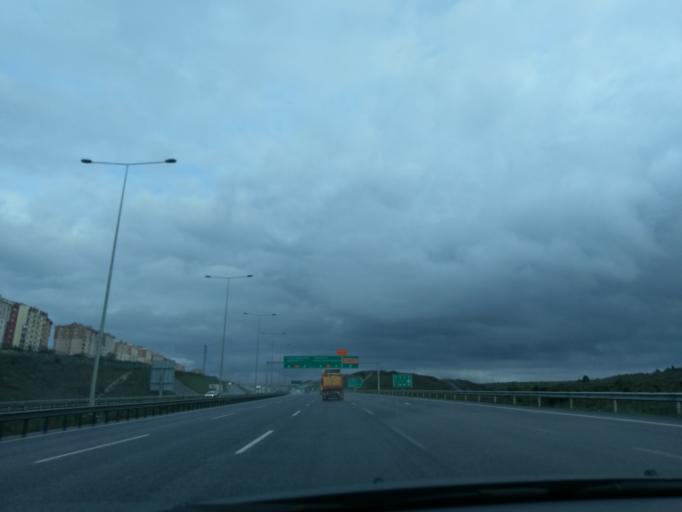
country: TR
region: Istanbul
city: Basaksehir
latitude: 41.0871
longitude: 28.8137
